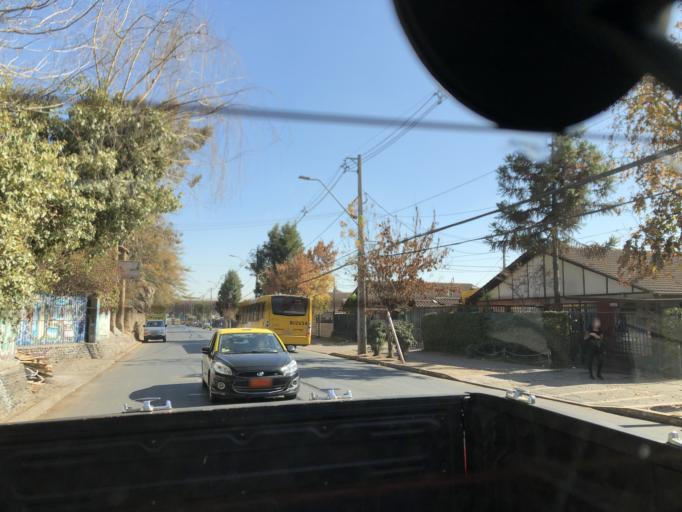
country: CL
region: Santiago Metropolitan
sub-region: Provincia de Cordillera
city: Puente Alto
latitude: -33.5691
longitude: -70.5803
